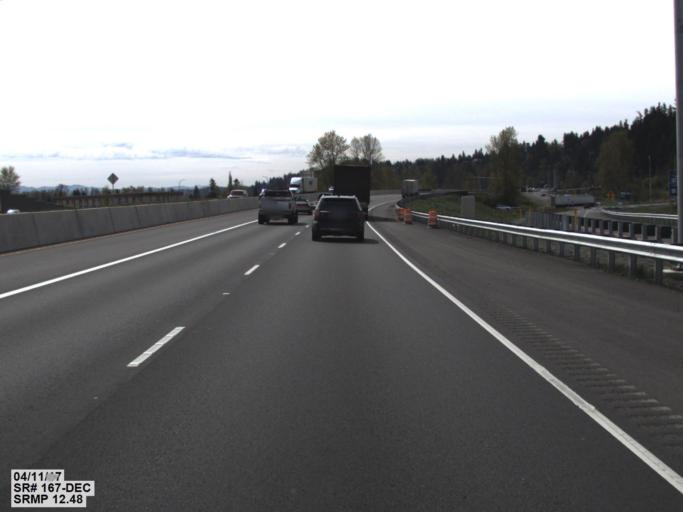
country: US
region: Washington
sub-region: King County
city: Algona
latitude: 47.2758
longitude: -122.2586
